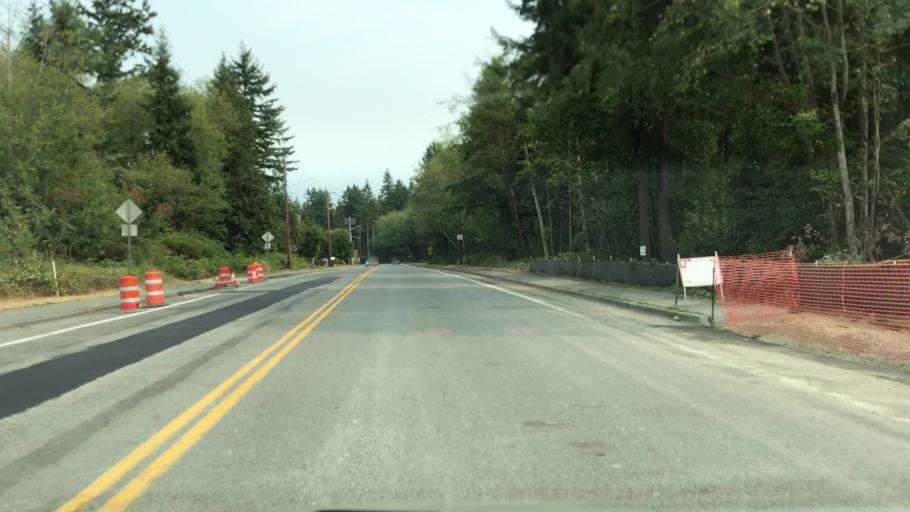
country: US
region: Washington
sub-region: Snohomish County
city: Martha Lake
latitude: 47.8802
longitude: -122.2327
